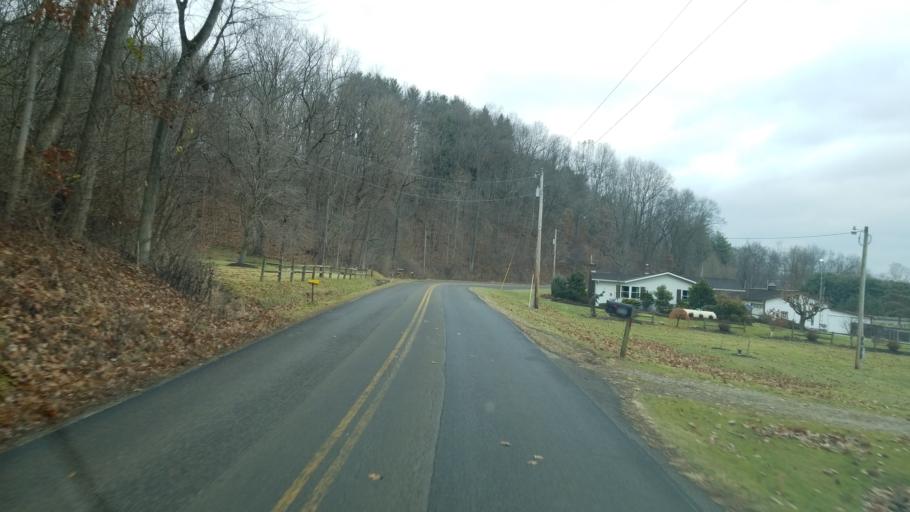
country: US
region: Ohio
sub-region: Holmes County
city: Millersburg
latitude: 40.6090
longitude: -81.9553
